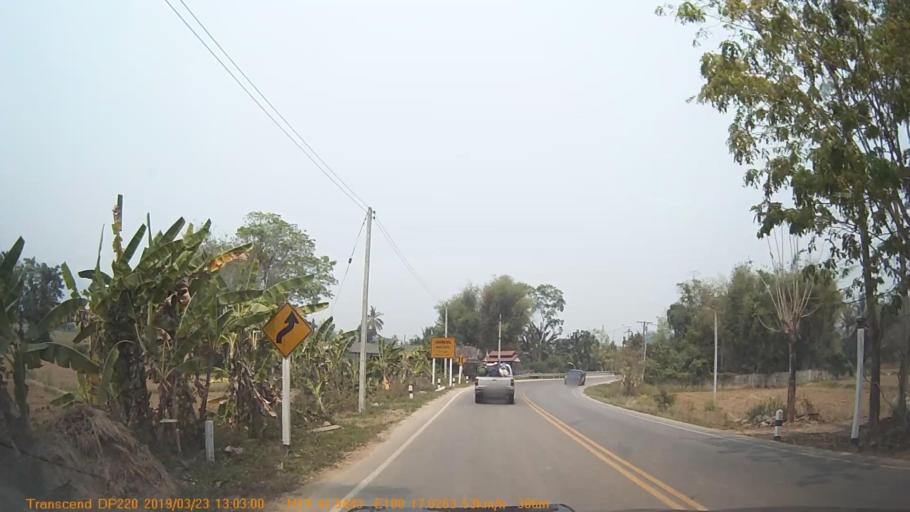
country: TH
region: Chiang Rai
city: Thoeng
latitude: 19.6992
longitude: 100.2838
